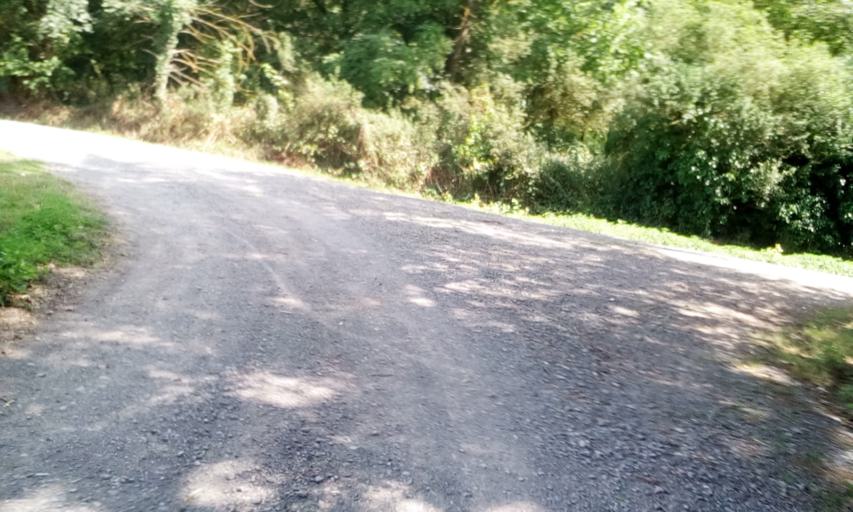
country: FR
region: Lower Normandy
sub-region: Departement du Calvados
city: Argences
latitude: 49.1411
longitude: -0.1667
